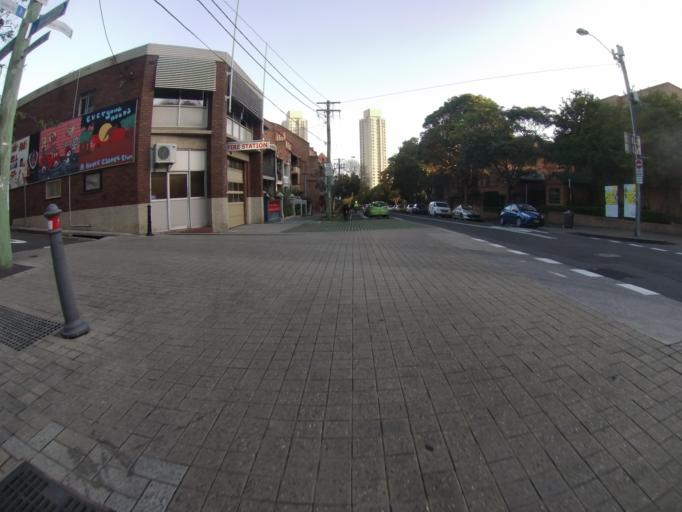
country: AU
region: New South Wales
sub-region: City of Sydney
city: Redfern
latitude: -33.8931
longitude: 151.2021
